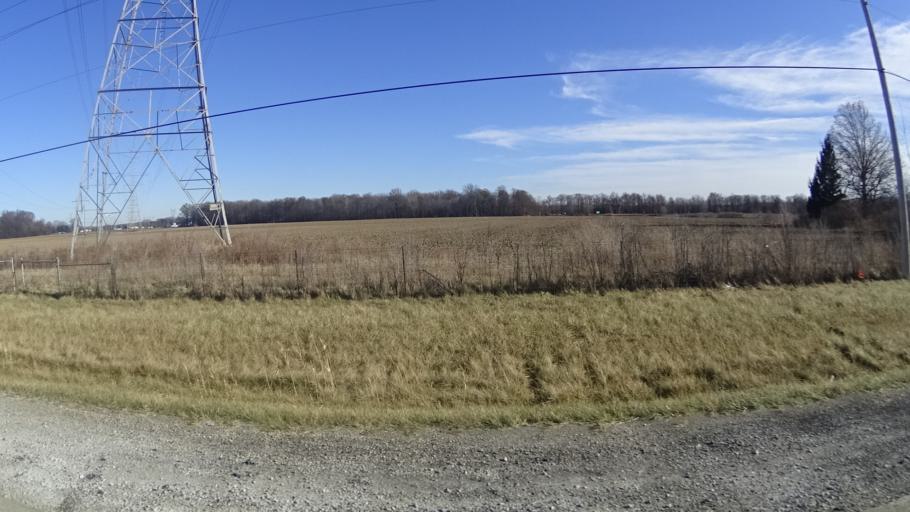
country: US
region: Ohio
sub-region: Lorain County
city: South Amherst
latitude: 41.3671
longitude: -82.2800
